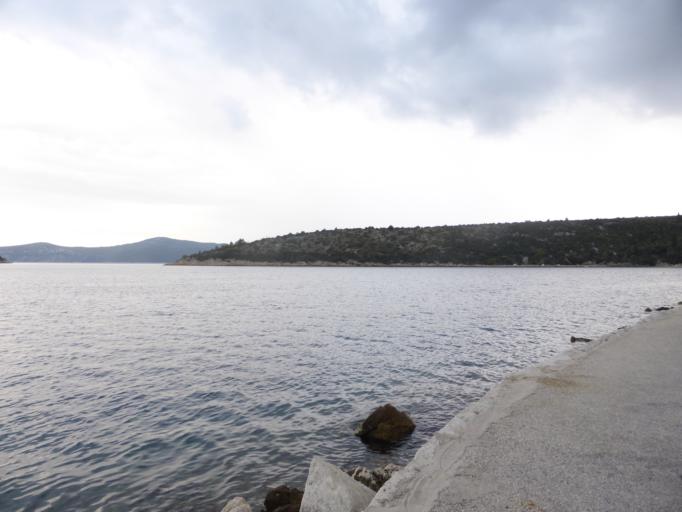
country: HR
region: Dubrovacko-Neretvanska
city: Podgora
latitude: 42.7800
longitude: 17.8745
